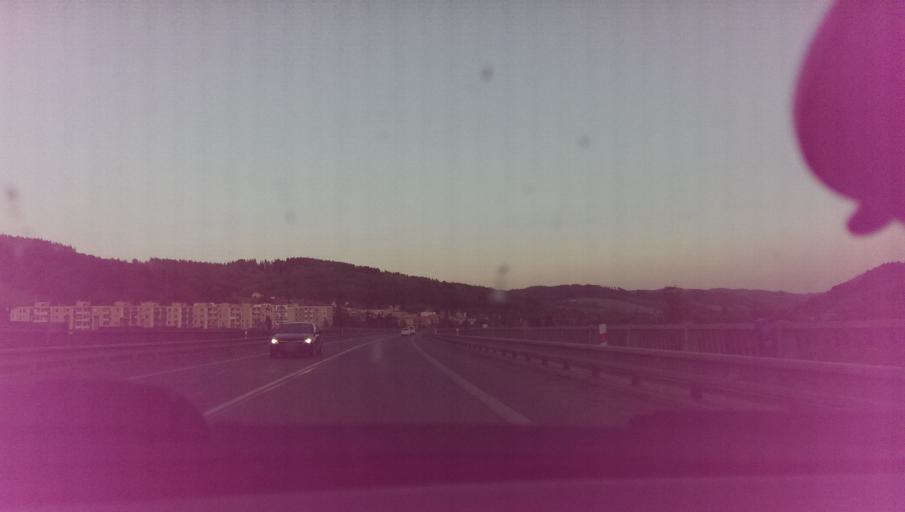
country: CZ
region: Zlin
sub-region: Okres Vsetin
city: Vsetin
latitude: 49.3297
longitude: 17.9985
